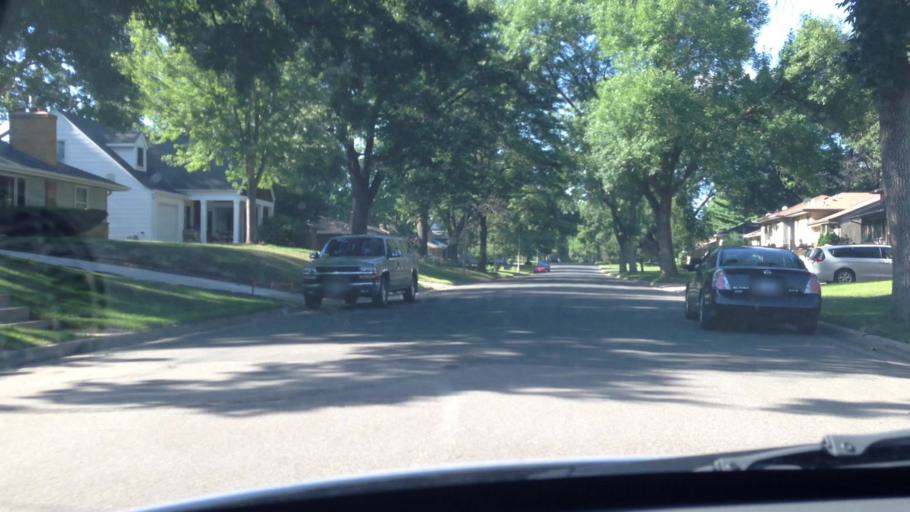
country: US
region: Minnesota
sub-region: Hennepin County
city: Richfield
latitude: 44.8782
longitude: -93.2984
